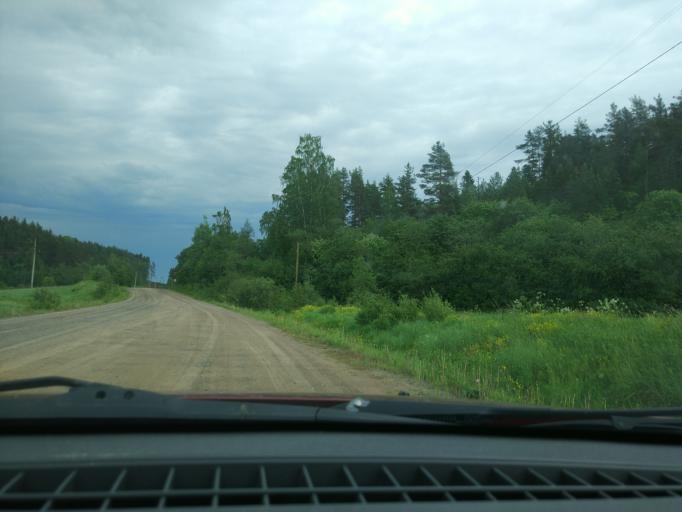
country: RU
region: Leningrad
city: Kuznechnoye
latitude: 61.2698
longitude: 29.8336
